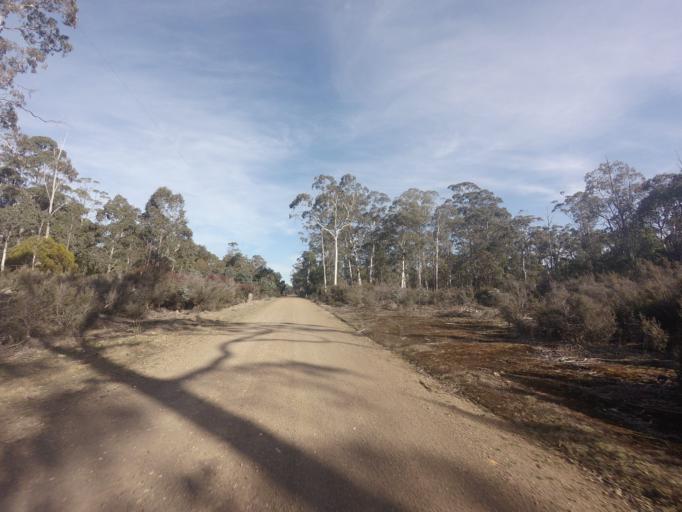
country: AU
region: Tasmania
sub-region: Sorell
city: Sorell
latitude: -42.5037
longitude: 147.4786
